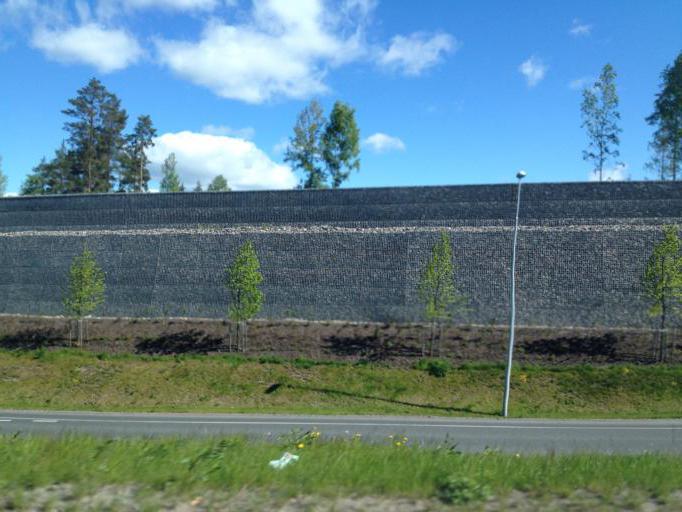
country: FI
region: Uusimaa
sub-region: Helsinki
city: Vantaa
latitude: 60.2299
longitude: 25.0576
